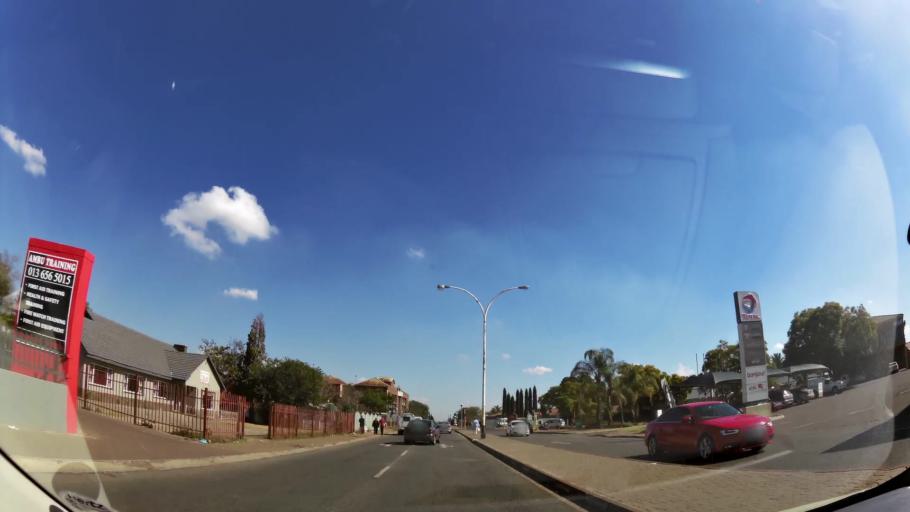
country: ZA
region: Mpumalanga
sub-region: Nkangala District Municipality
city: Witbank
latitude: -25.8753
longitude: 29.2298
